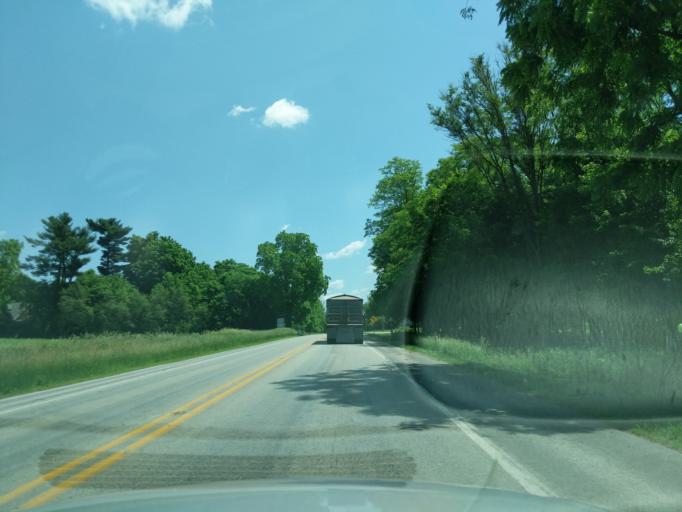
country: US
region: Indiana
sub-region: Noble County
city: Ligonier
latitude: 41.4744
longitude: -85.5837
